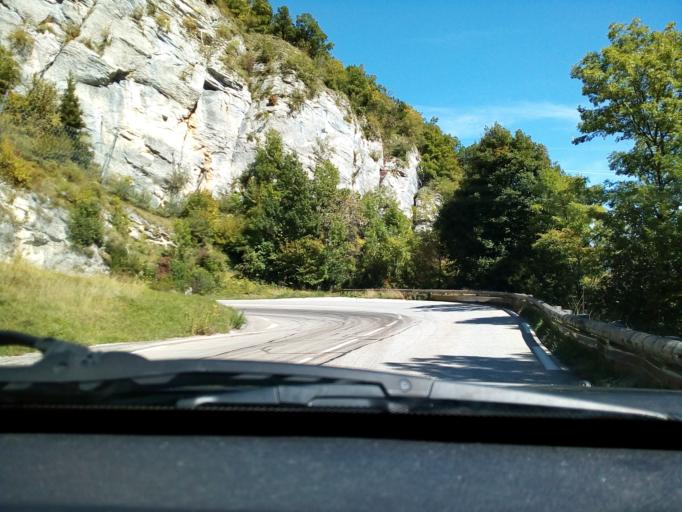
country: FR
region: Rhone-Alpes
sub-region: Departement de l'Isere
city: Sassenage
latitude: 45.2058
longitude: 5.6351
